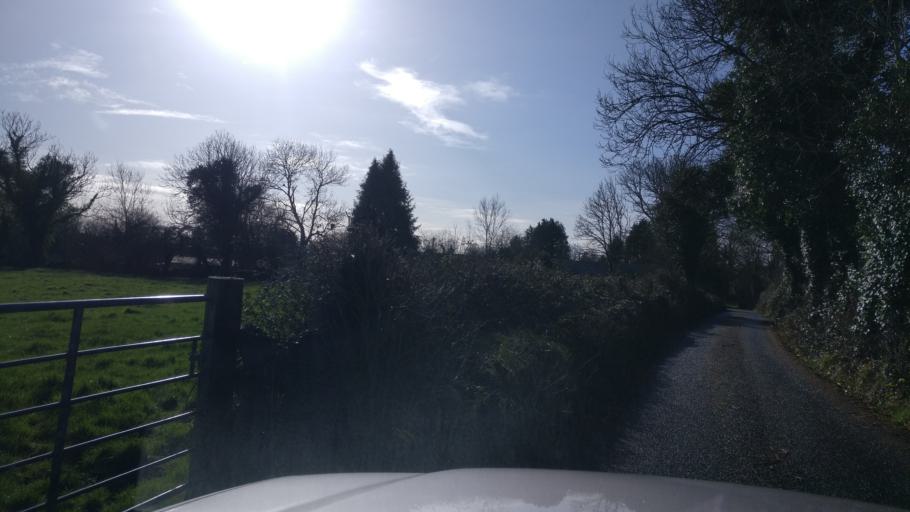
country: IE
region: Connaught
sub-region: County Galway
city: Athenry
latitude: 53.2347
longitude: -8.7792
